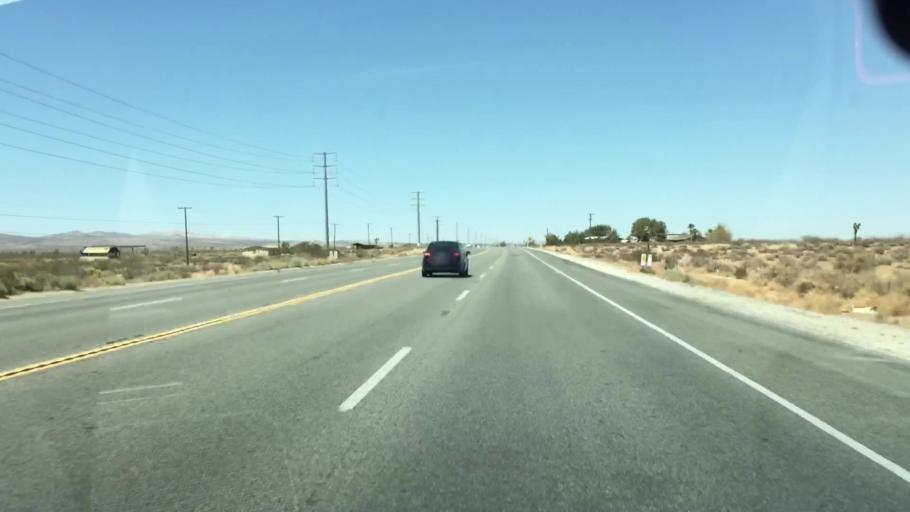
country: US
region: California
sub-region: San Bernardino County
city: Adelanto
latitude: 34.5980
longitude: -117.4184
